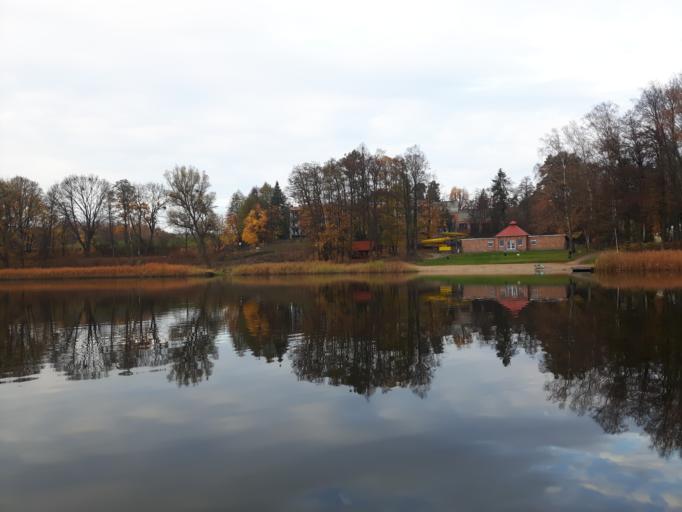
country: PL
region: Warmian-Masurian Voivodeship
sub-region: Powiat olsztynski
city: Barczewo
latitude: 53.8284
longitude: 20.7375
